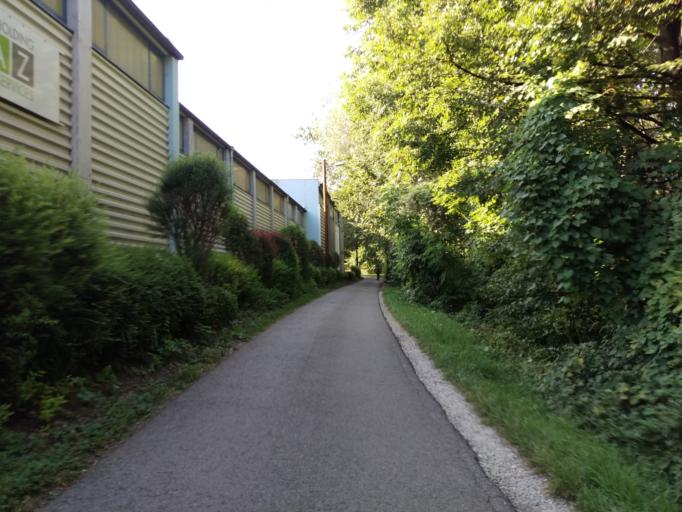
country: AT
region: Styria
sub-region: Graz Stadt
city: Graz
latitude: 47.0483
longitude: 15.4399
